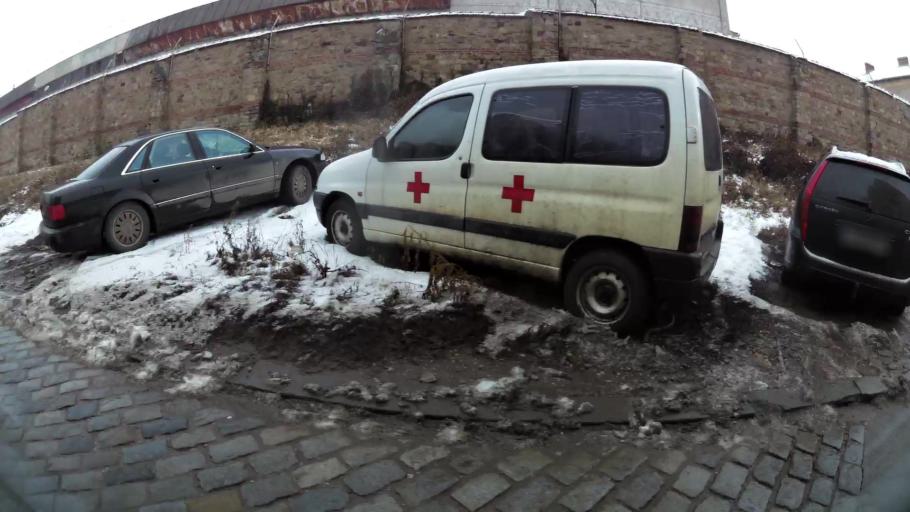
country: BG
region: Sofia-Capital
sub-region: Stolichna Obshtina
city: Sofia
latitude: 42.7089
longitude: 23.3022
